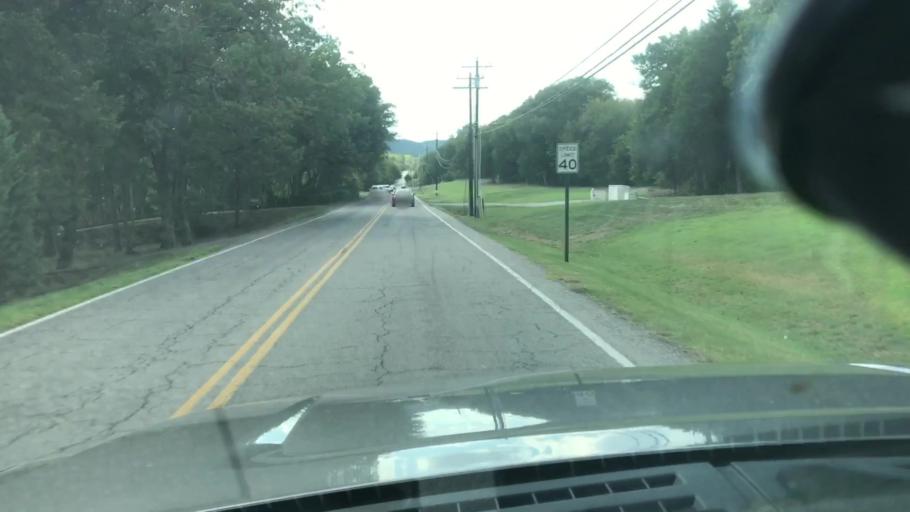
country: US
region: Tennessee
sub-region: Davidson County
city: Forest Hills
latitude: 36.0259
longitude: -86.8939
